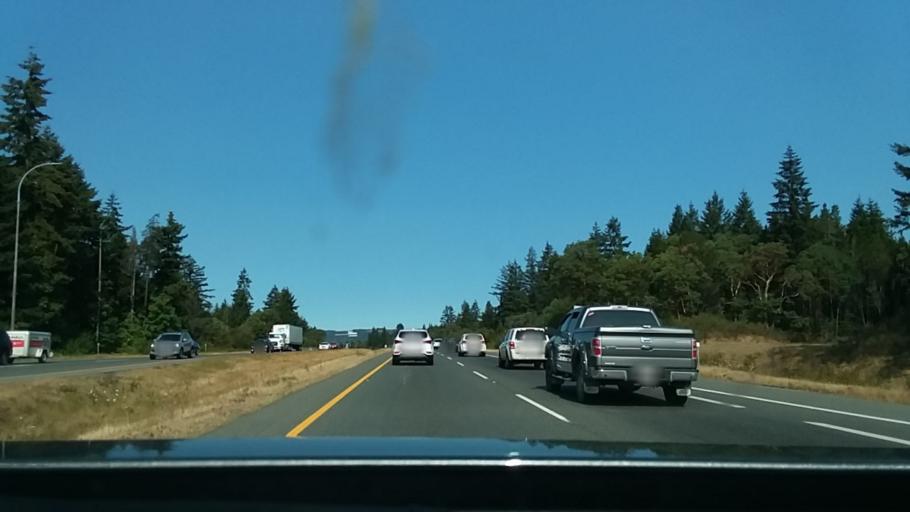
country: CA
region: British Columbia
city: Nanaimo
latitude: 49.1895
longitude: -124.0052
